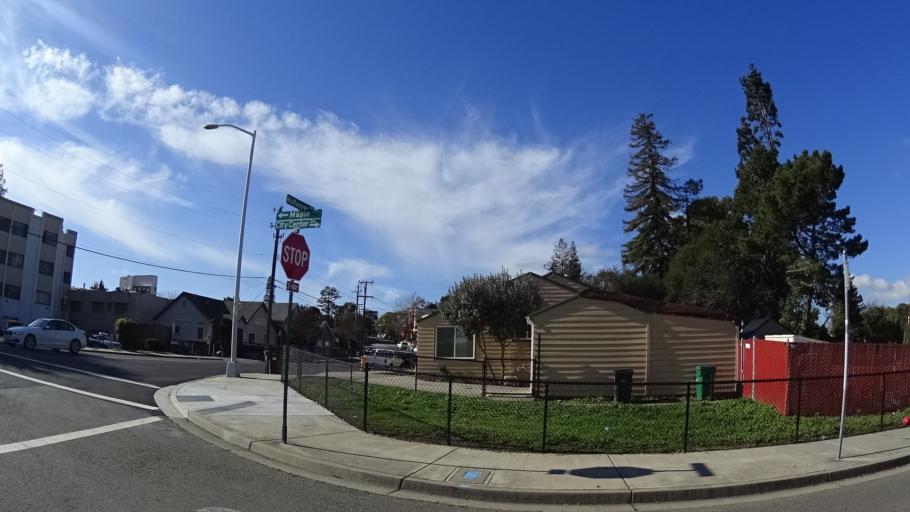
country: US
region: California
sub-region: Alameda County
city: Hayward
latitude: 37.6764
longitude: -122.0837
